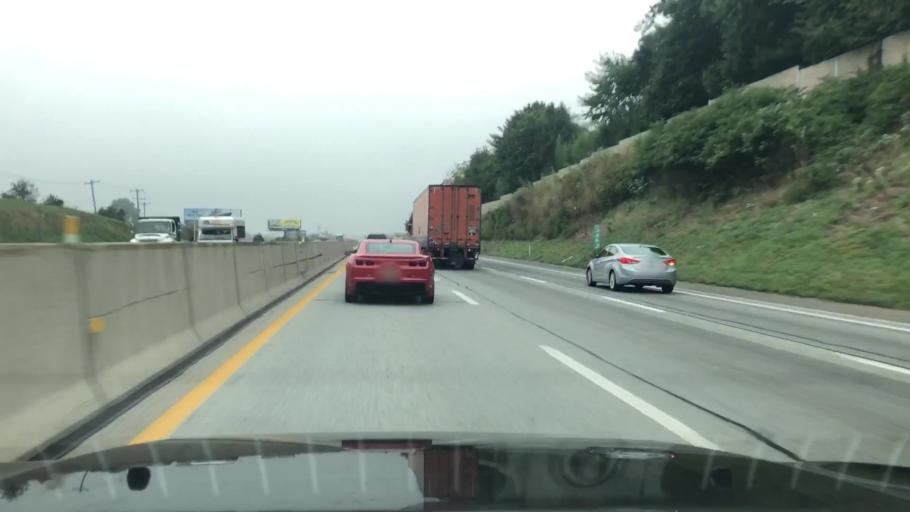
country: US
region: Pennsylvania
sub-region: Bucks County
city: Warminster Heights
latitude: 40.1635
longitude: -75.0581
